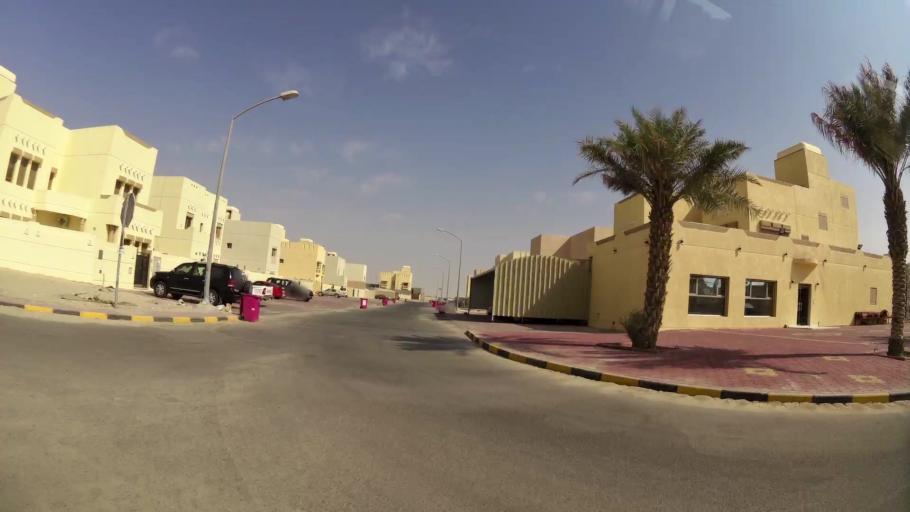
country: KW
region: Al Ahmadi
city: Al Wafrah
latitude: 28.8061
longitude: 48.0629
